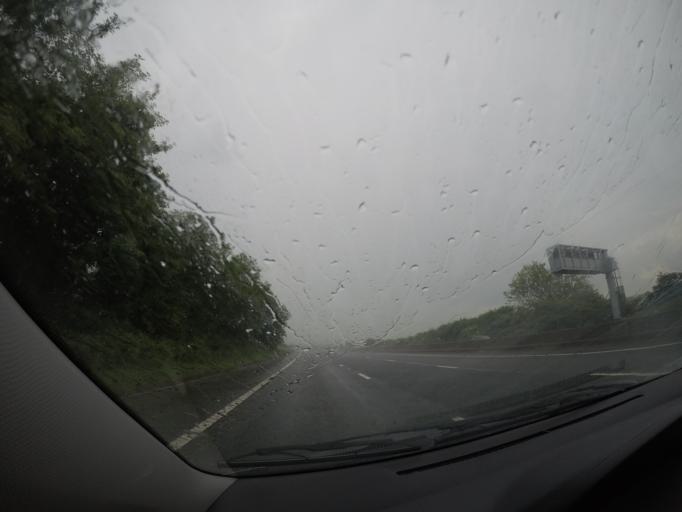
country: GB
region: England
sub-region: Cumbria
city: Penrith
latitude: 54.6706
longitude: -2.7755
